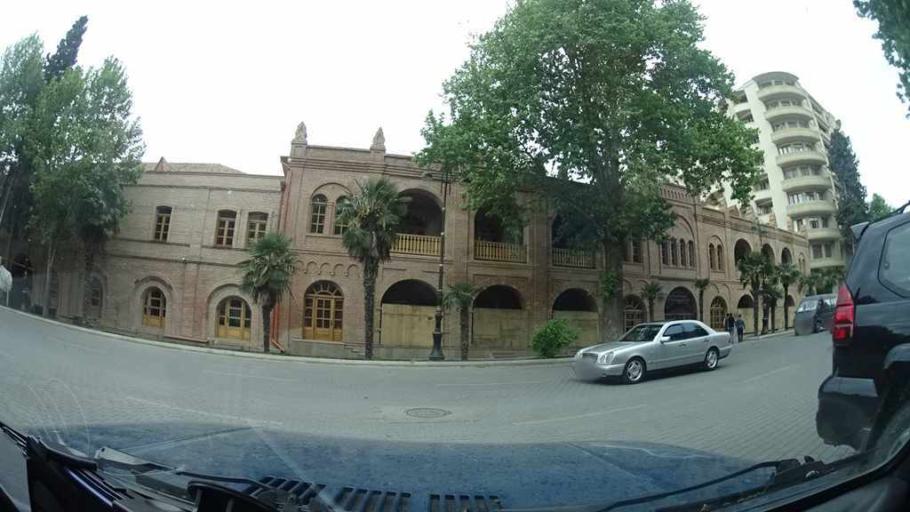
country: AZ
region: Ganja City
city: Ganja
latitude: 40.6796
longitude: 46.3615
